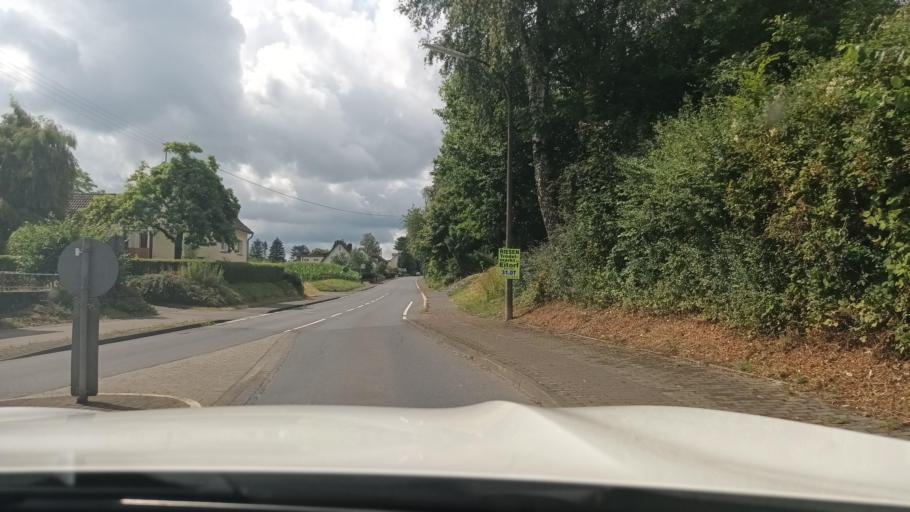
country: DE
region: North Rhine-Westphalia
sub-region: Regierungsbezirk Koln
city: Eitorf
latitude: 50.7560
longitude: 7.4318
